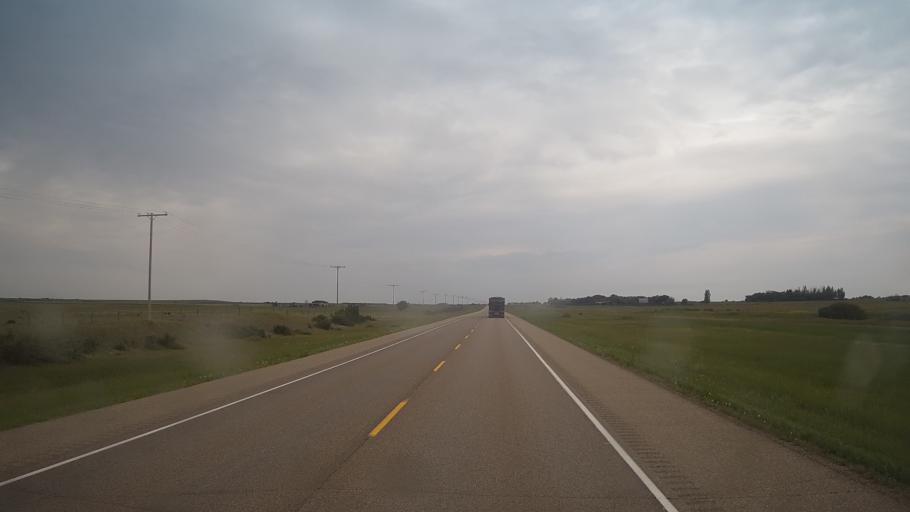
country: CA
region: Saskatchewan
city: Langham
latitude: 52.1289
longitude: -107.1564
